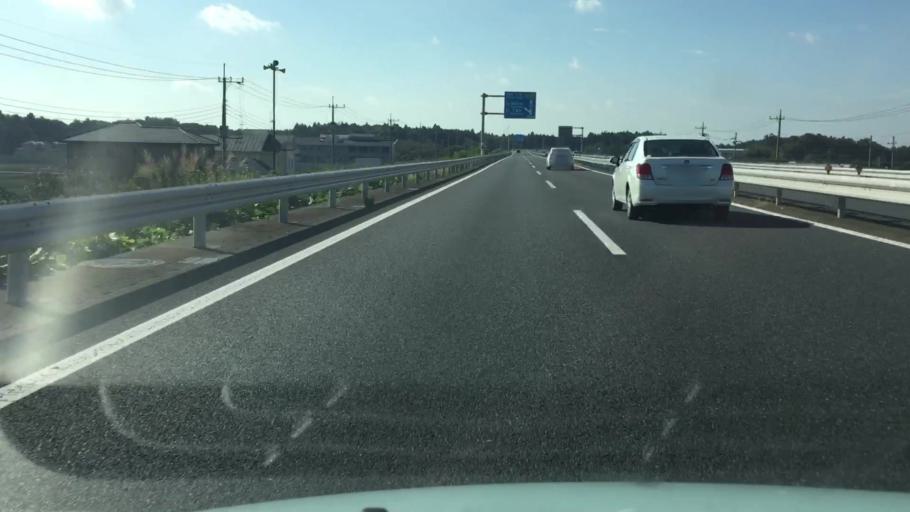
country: JP
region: Tochigi
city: Mooka
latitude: 36.4771
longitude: 139.9907
